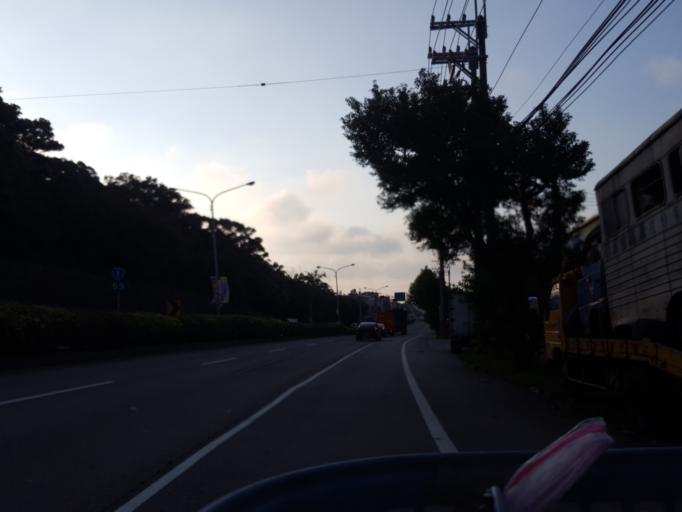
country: TW
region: Taiwan
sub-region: Hsinchu
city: Zhubei
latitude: 24.8778
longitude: 121.0444
